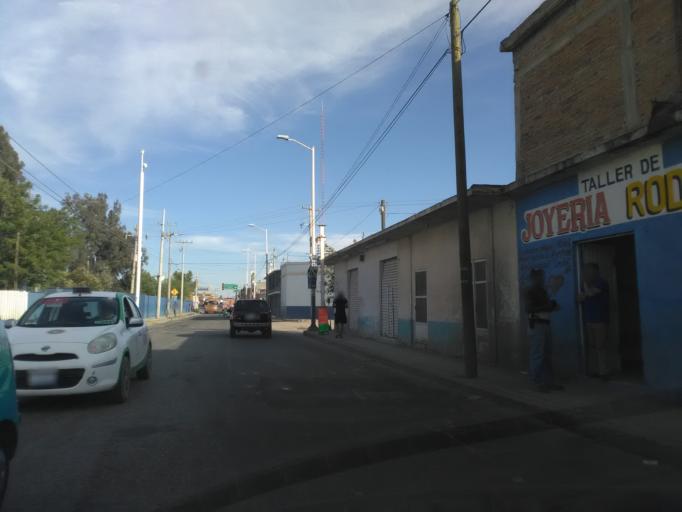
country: MX
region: Durango
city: Victoria de Durango
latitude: 24.0227
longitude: -104.6262
